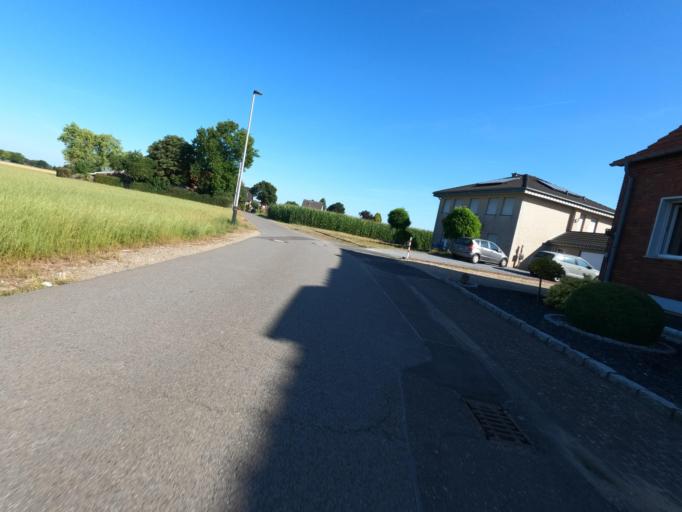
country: DE
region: North Rhine-Westphalia
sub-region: Regierungsbezirk Koln
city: Heinsberg
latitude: 51.0782
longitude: 6.1226
